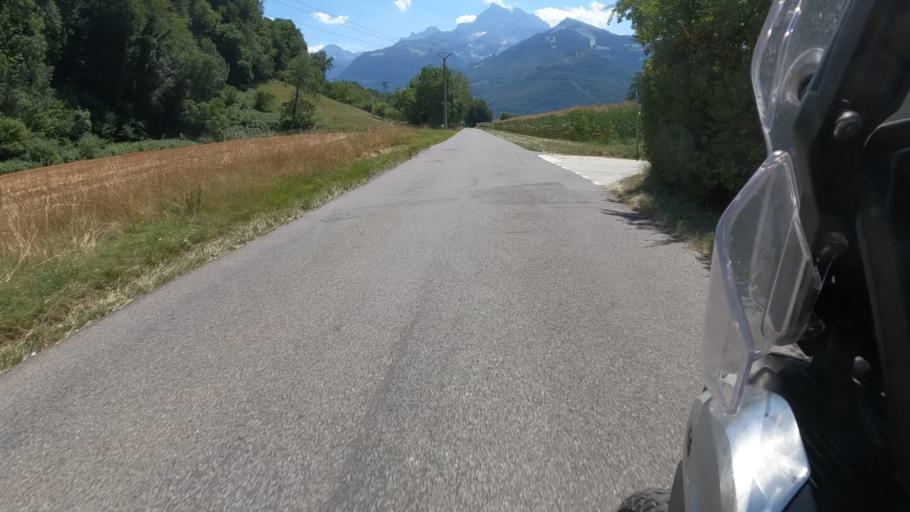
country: CH
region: Vaud
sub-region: Aigle District
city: Bex
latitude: 46.2663
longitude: 7.0057
